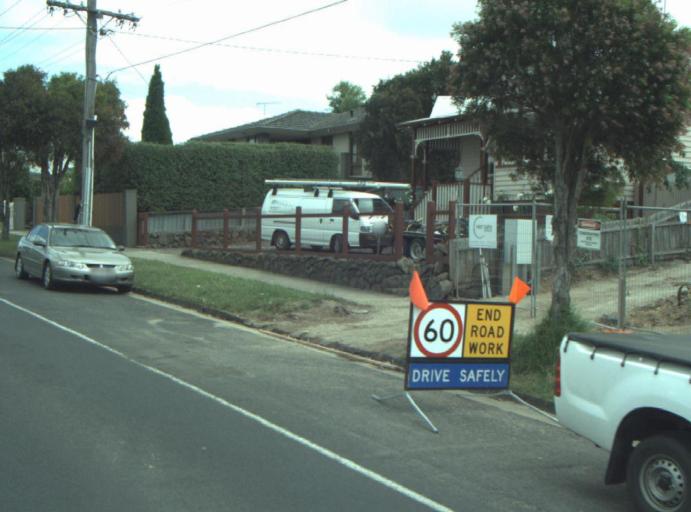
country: AU
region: Victoria
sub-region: Greater Geelong
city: Geelong West
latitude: -38.1591
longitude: 144.3407
